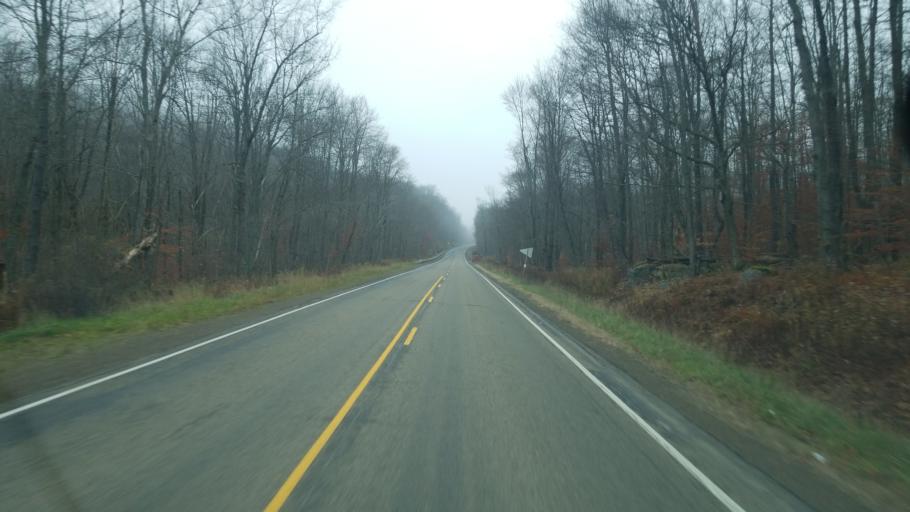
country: US
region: Pennsylvania
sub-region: McKean County
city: Smethport
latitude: 41.8064
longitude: -78.5118
